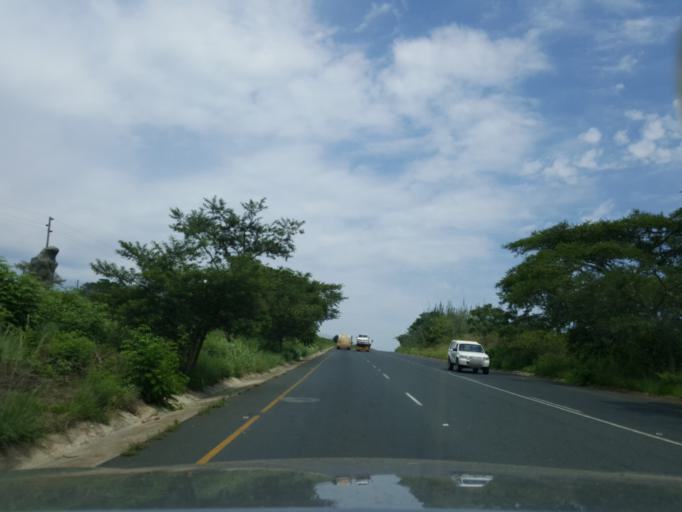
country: ZA
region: Mpumalanga
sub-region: Ehlanzeni District
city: White River
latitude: -25.3735
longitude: 31.0790
